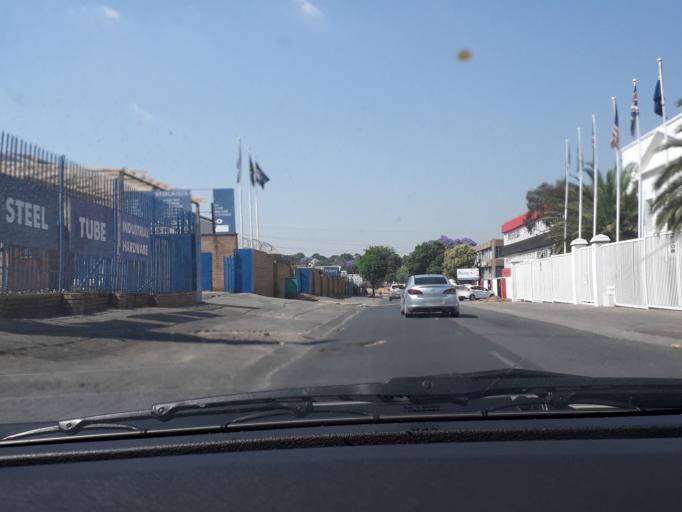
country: ZA
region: Gauteng
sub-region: City of Johannesburg Metropolitan Municipality
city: Modderfontein
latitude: -26.1133
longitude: 28.0811
